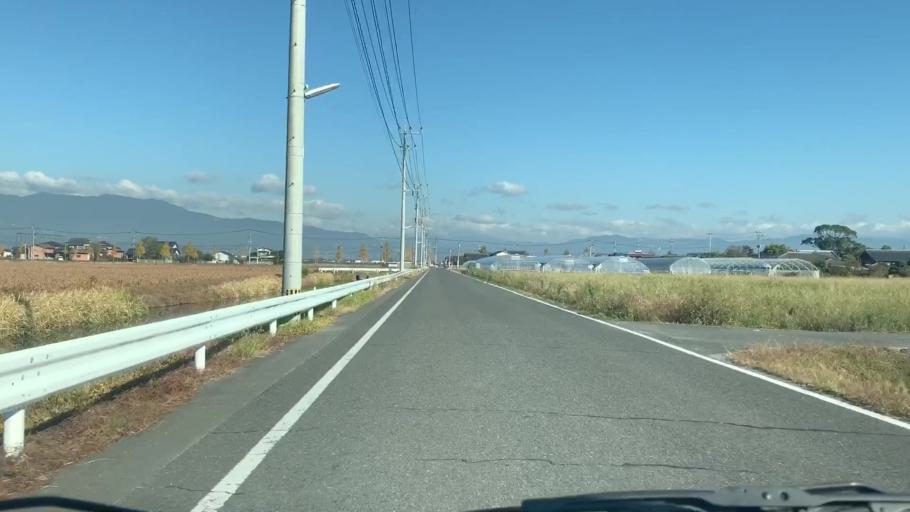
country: JP
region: Saga Prefecture
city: Saga-shi
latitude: 33.2519
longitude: 130.2579
